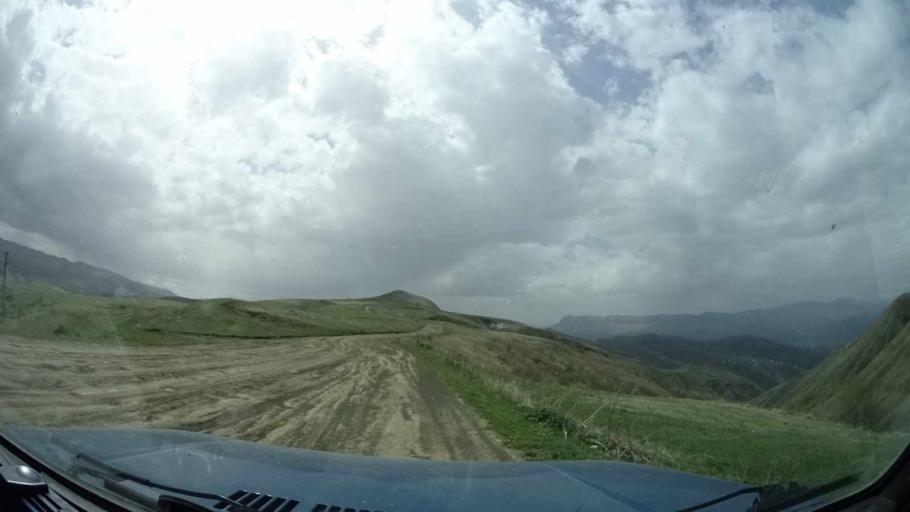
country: RU
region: Dagestan
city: Kubachi
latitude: 42.0813
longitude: 47.5541
